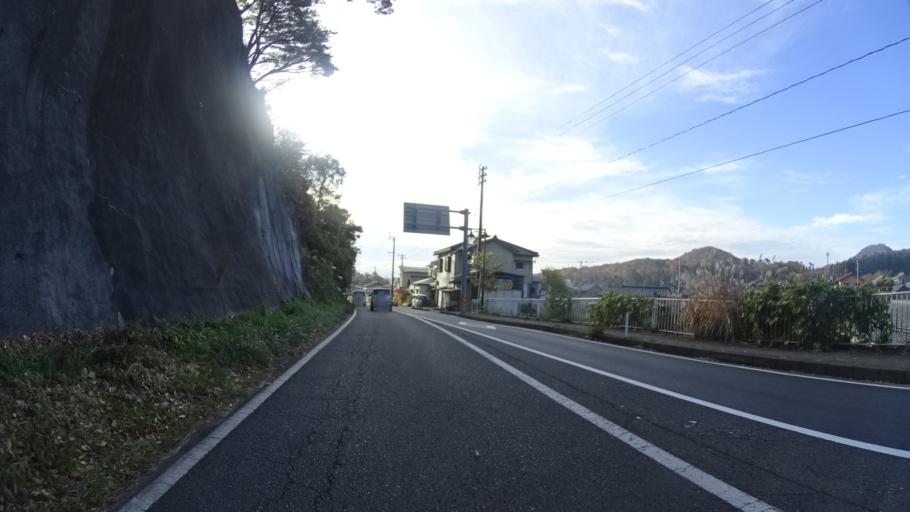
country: JP
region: Niigata
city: Yoshida-kasugacho
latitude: 37.7036
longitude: 138.8312
